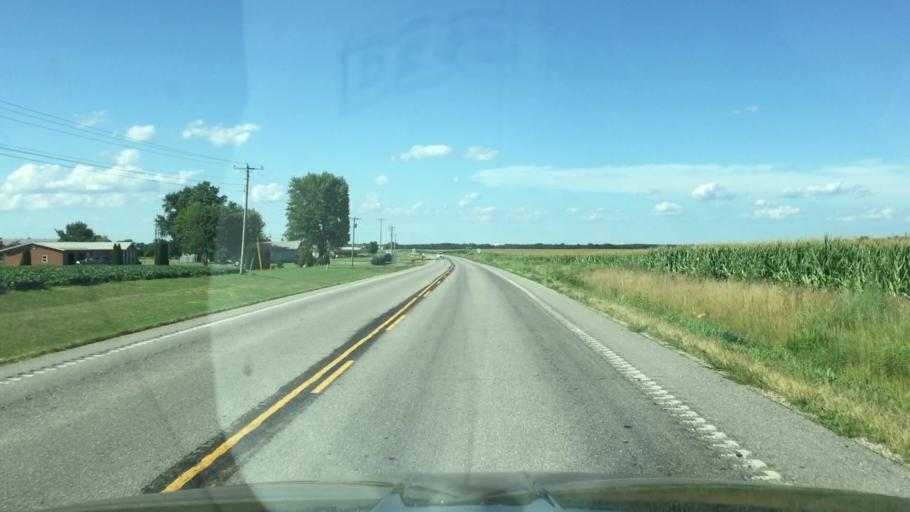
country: US
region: Missouri
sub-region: Moniteau County
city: Tipton
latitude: 38.5747
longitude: -92.7936
